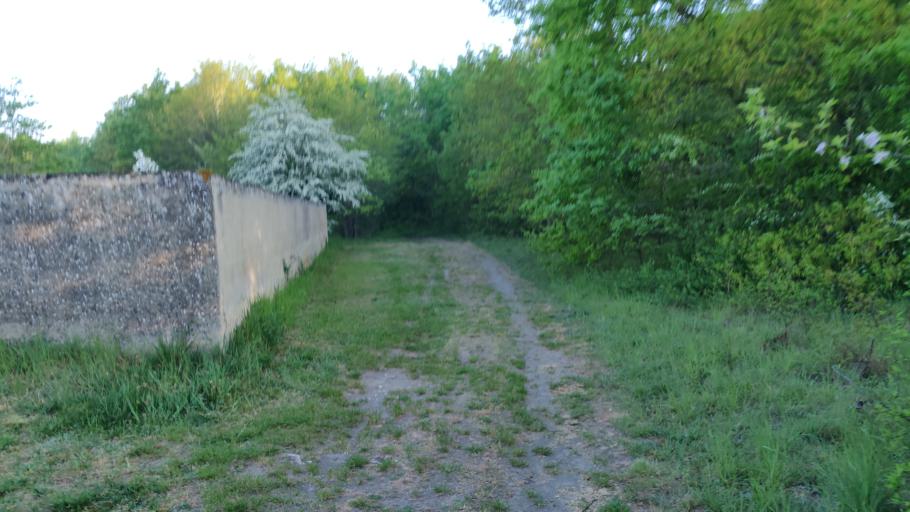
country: FR
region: Ile-de-France
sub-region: Departement des Yvelines
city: Freneuse
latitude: 49.0399
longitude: 1.6301
